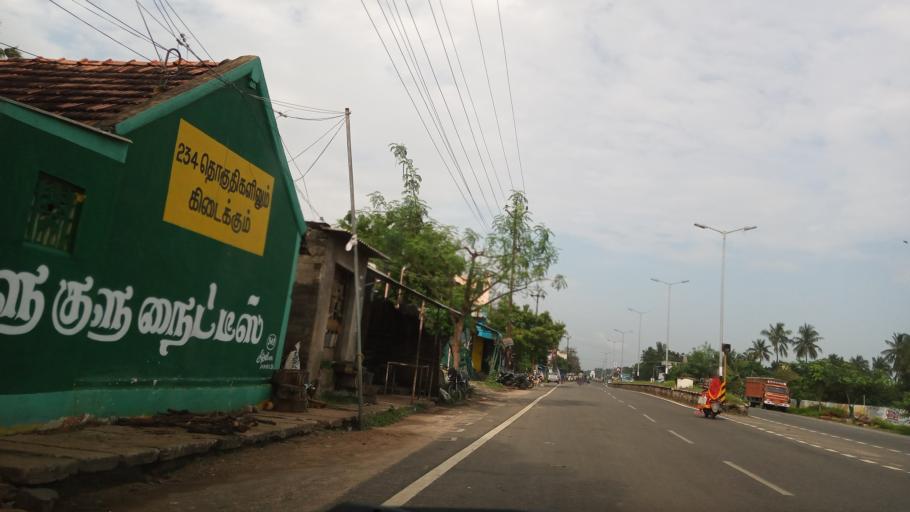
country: IN
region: Tamil Nadu
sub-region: Villupuram
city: Auroville
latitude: 12.0338
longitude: 79.8651
